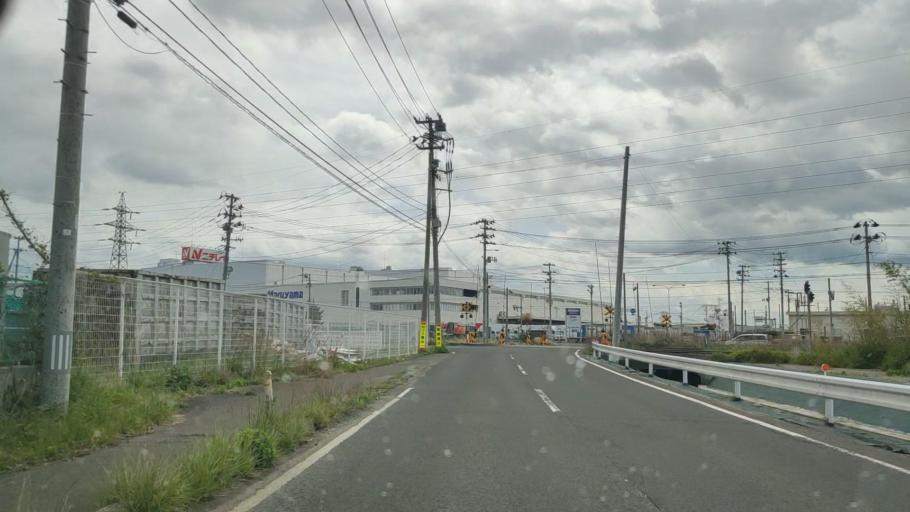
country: JP
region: Miyagi
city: Shiogama
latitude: 38.2774
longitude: 141.0100
